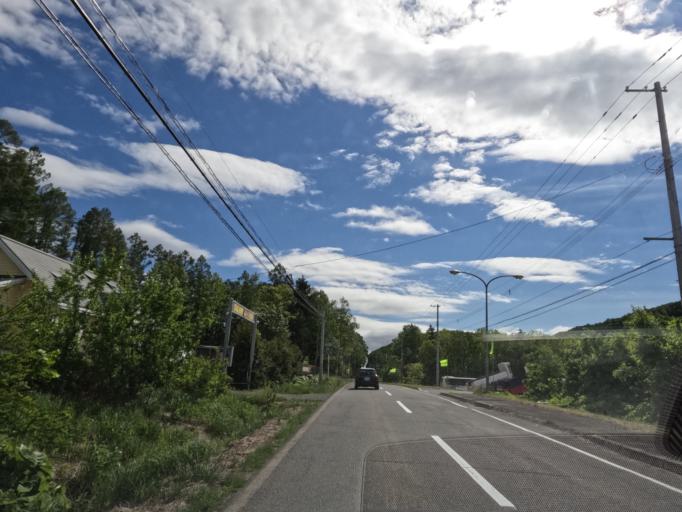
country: JP
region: Hokkaido
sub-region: Asahikawa-shi
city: Asahikawa
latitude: 43.8381
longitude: 142.5414
